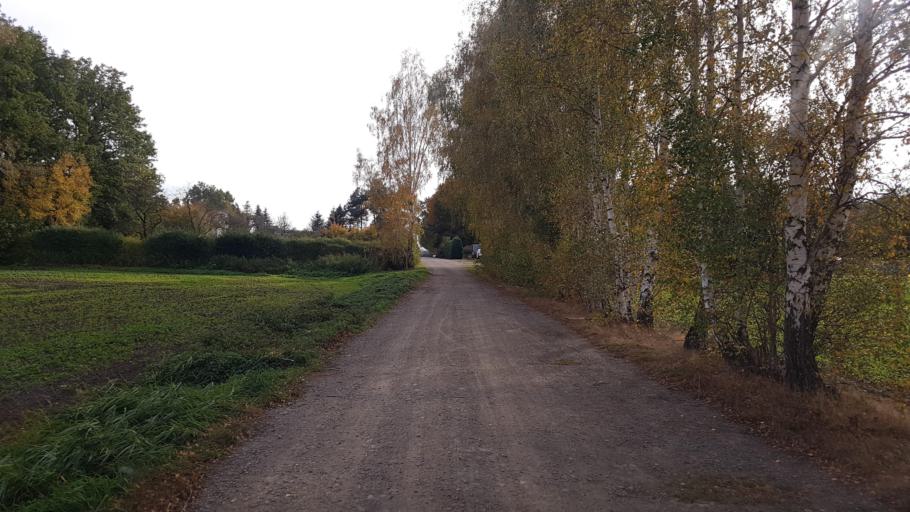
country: DE
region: Brandenburg
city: Schraden
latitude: 51.4417
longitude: 13.6929
